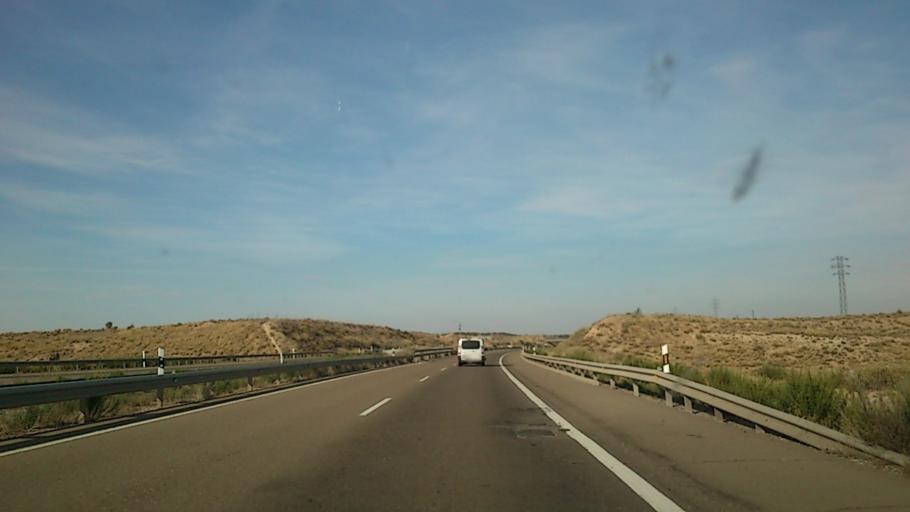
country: ES
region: Aragon
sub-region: Provincia de Zaragoza
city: Maria de Huerva
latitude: 41.5405
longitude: -1.0051
